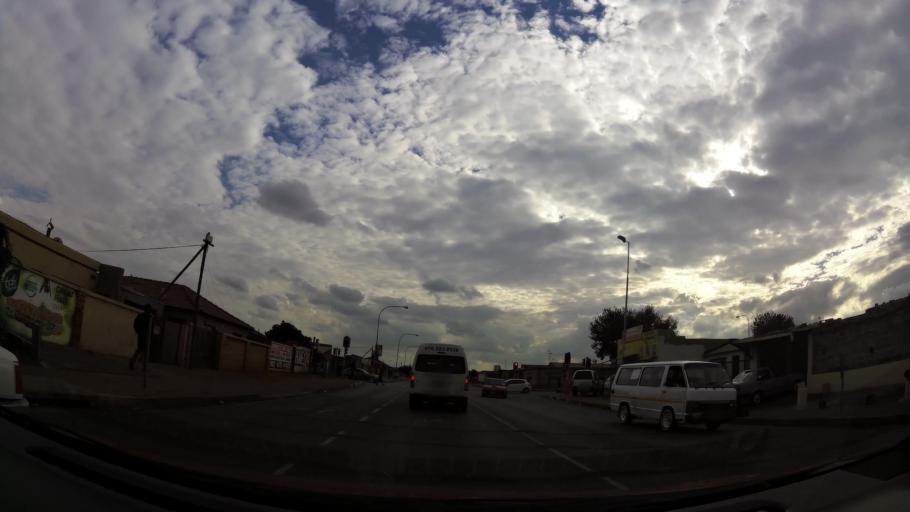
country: ZA
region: Gauteng
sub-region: City of Johannesburg Metropolitan Municipality
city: Soweto
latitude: -26.2487
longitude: 27.8319
